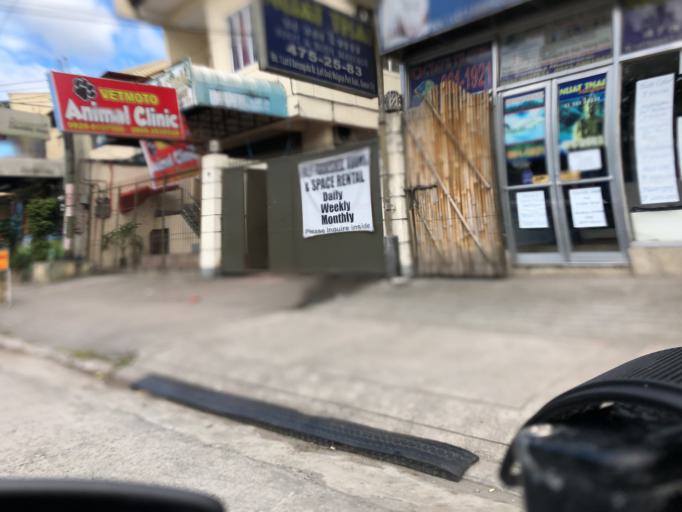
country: PH
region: Central Luzon
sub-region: Province of Bulacan
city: San Jose del Monte
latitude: 14.7402
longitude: 121.0560
